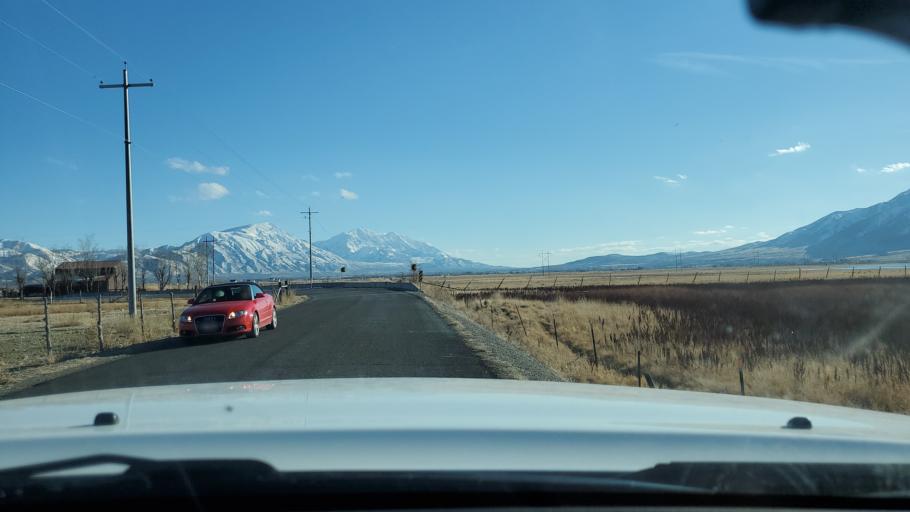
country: US
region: Utah
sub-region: Utah County
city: Benjamin
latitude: 40.1156
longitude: -111.7691
